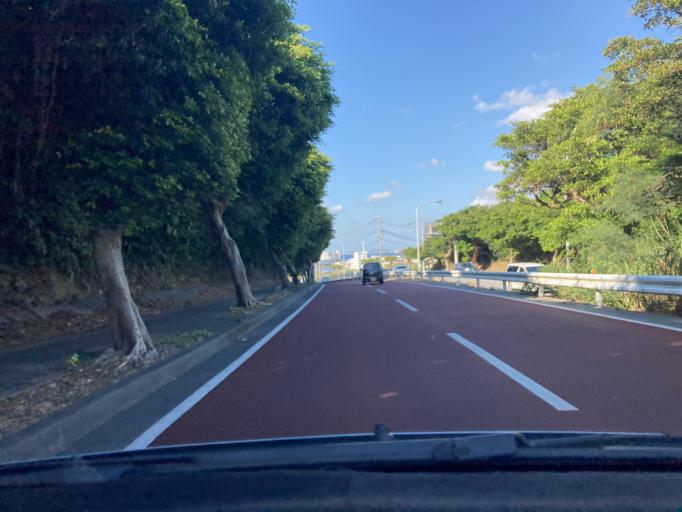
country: JP
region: Okinawa
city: Ginowan
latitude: 26.2579
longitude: 127.7281
